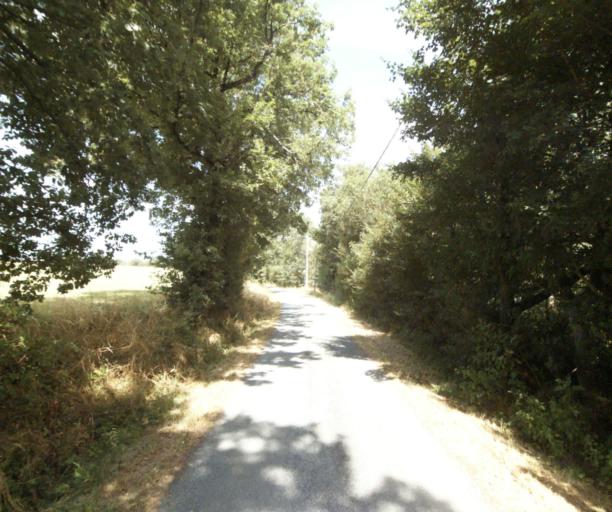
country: FR
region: Midi-Pyrenees
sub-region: Departement du Tarn
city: Dourgne
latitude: 43.4878
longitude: 2.1082
